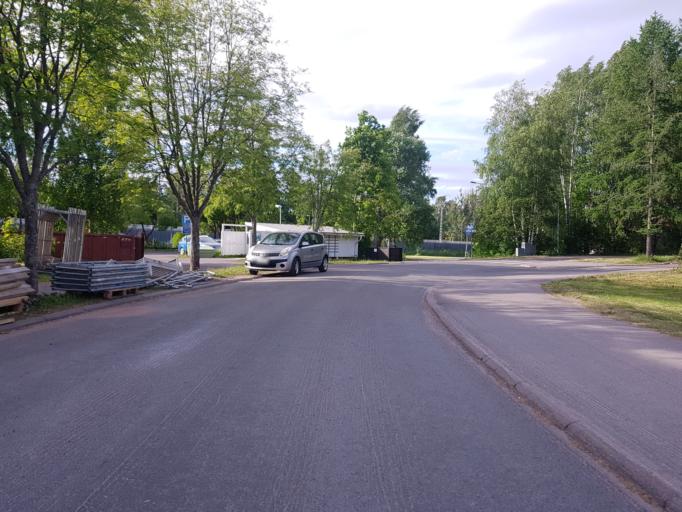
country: FI
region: Uusimaa
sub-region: Helsinki
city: Helsinki
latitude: 60.2243
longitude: 24.9606
